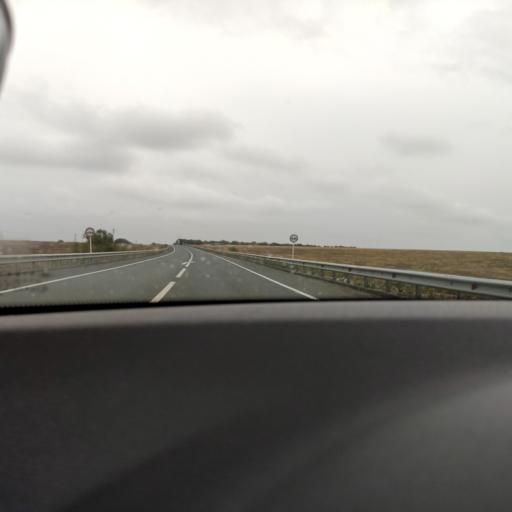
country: RU
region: Samara
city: Mirnyy
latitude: 53.5928
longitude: 50.2793
